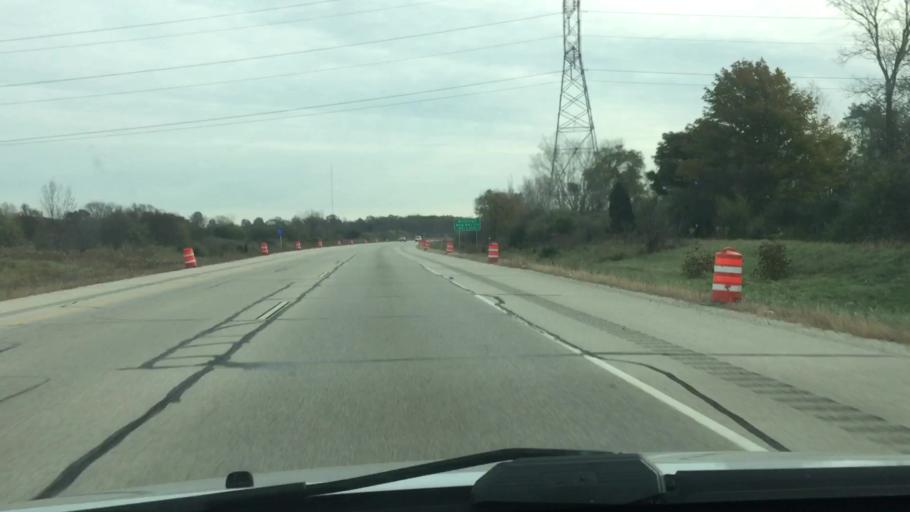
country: US
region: Wisconsin
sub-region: Waukesha County
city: Big Bend
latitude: 42.9255
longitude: -88.1870
